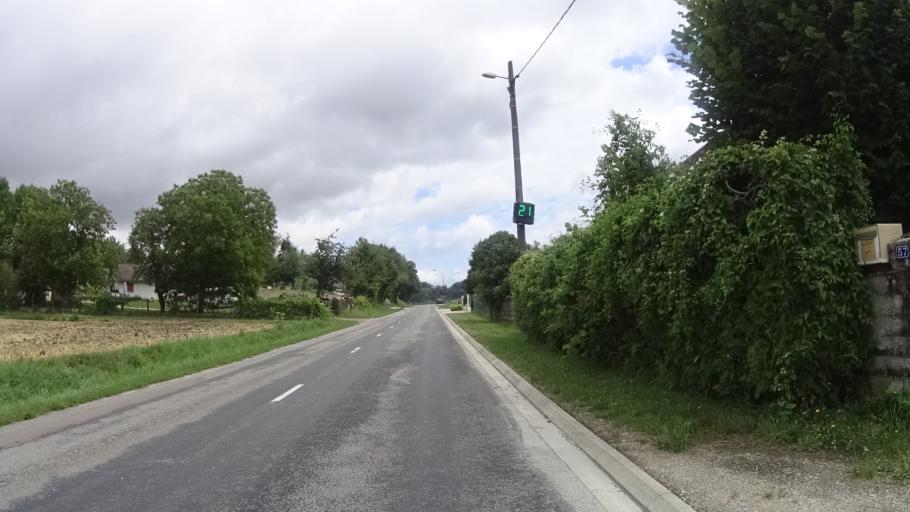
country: FR
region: Champagne-Ardenne
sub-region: Departement de l'Aube
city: Bouilly
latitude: 48.1180
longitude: 3.9826
